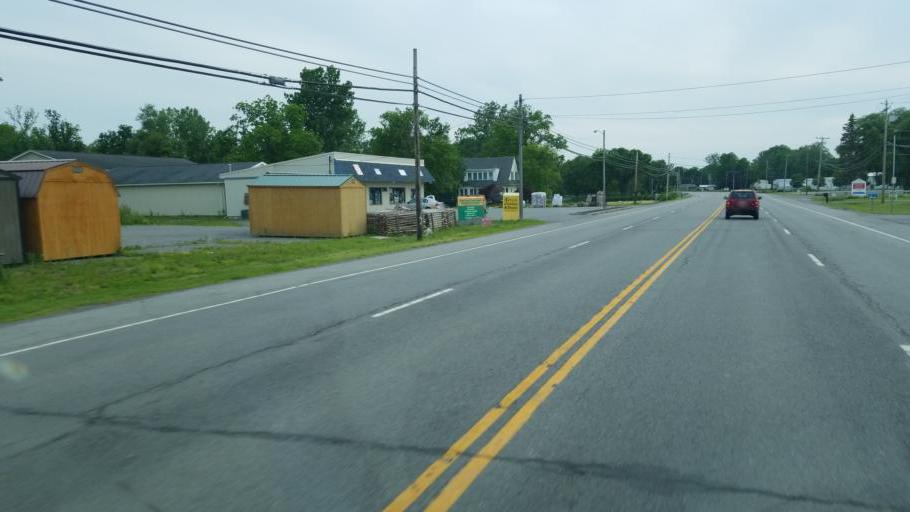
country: US
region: New York
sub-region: Genesee County
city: Batavia
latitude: 43.0073
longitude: -78.2261
